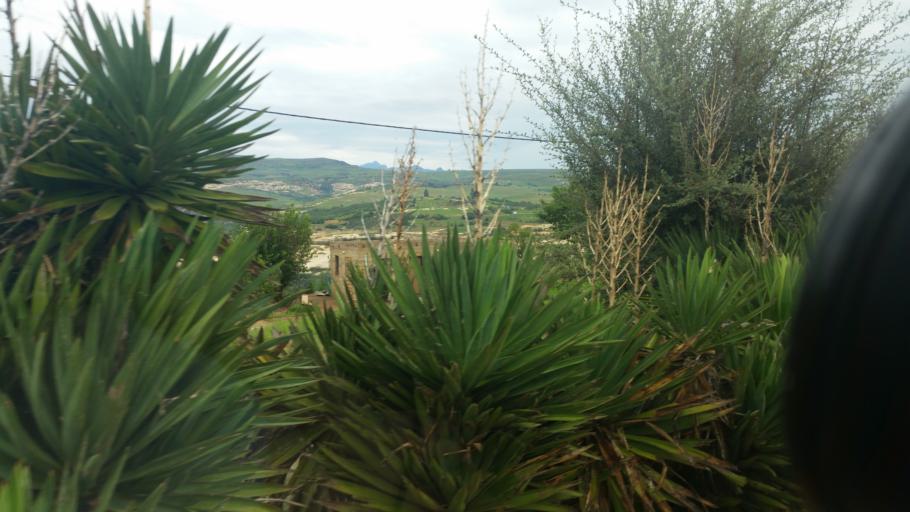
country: LS
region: Berea
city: Teyateyaneng
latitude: -29.1199
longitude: 27.9616
